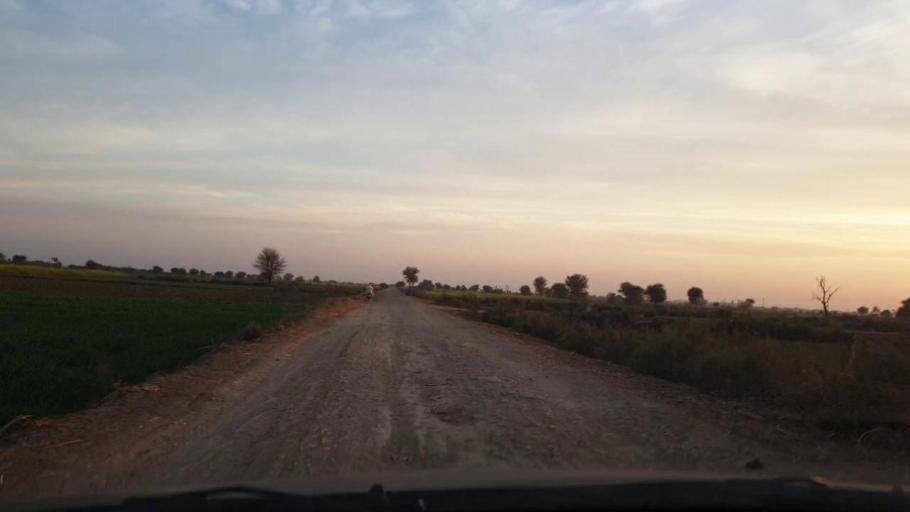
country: PK
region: Sindh
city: Sinjhoro
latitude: 26.0988
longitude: 68.7969
